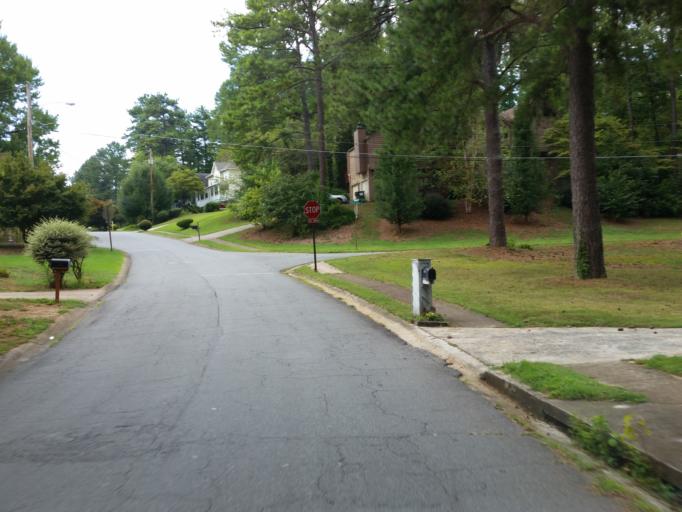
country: US
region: Georgia
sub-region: Cobb County
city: Marietta
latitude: 34.0246
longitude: -84.5407
